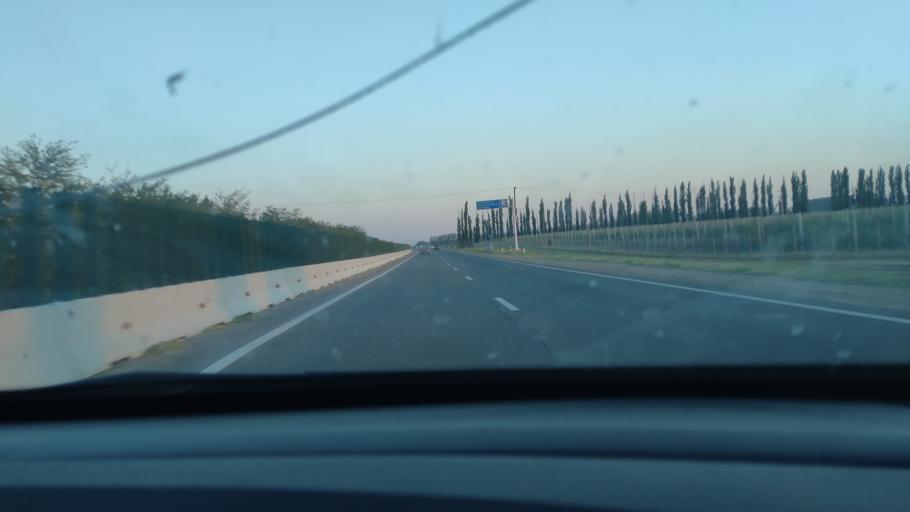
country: RU
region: Krasnodarskiy
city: Timashevsk
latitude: 45.5819
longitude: 38.9166
